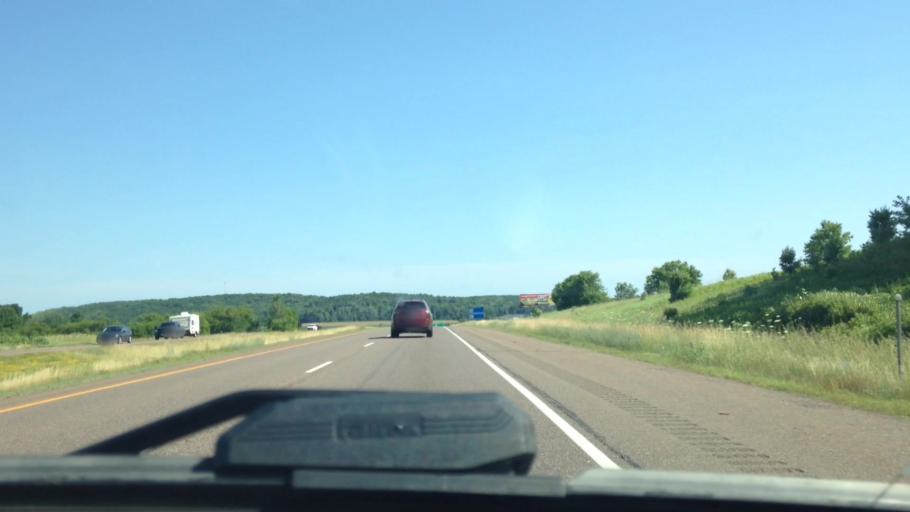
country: US
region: Wisconsin
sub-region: Chippewa County
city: Chippewa Falls
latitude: 44.9554
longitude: -91.4256
